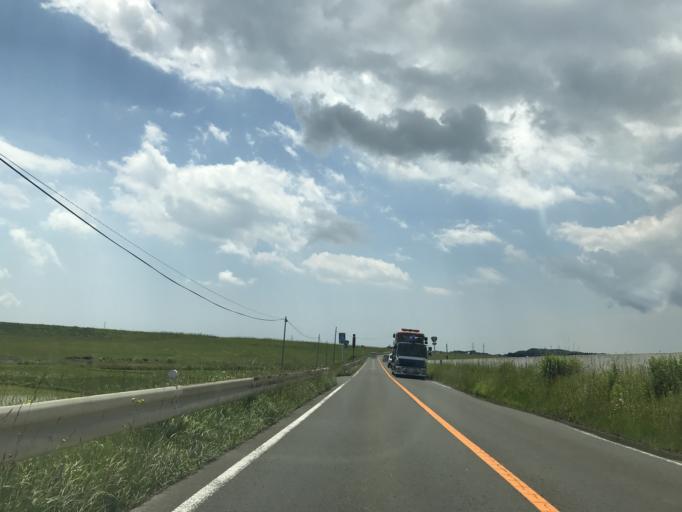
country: JP
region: Miyagi
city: Matsushima
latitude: 38.4448
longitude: 141.0803
